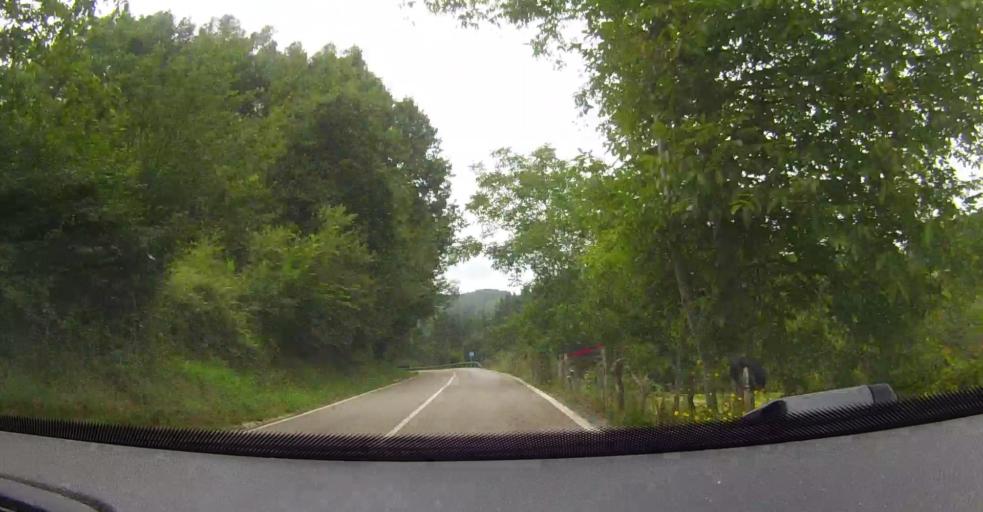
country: ES
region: Basque Country
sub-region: Bizkaia
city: Balmaseda
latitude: 43.2450
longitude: -3.2687
